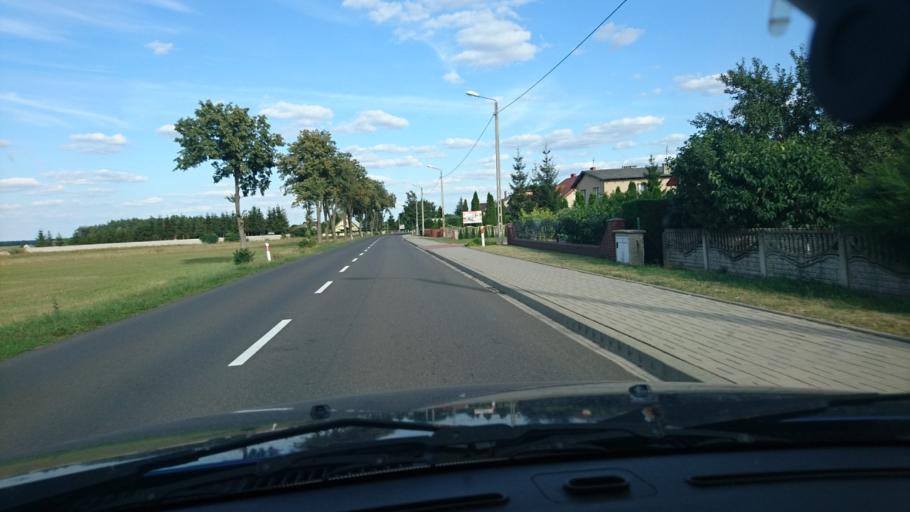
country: PL
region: Greater Poland Voivodeship
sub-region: Powiat krotoszynski
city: Sulmierzyce
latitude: 51.6152
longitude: 17.5081
